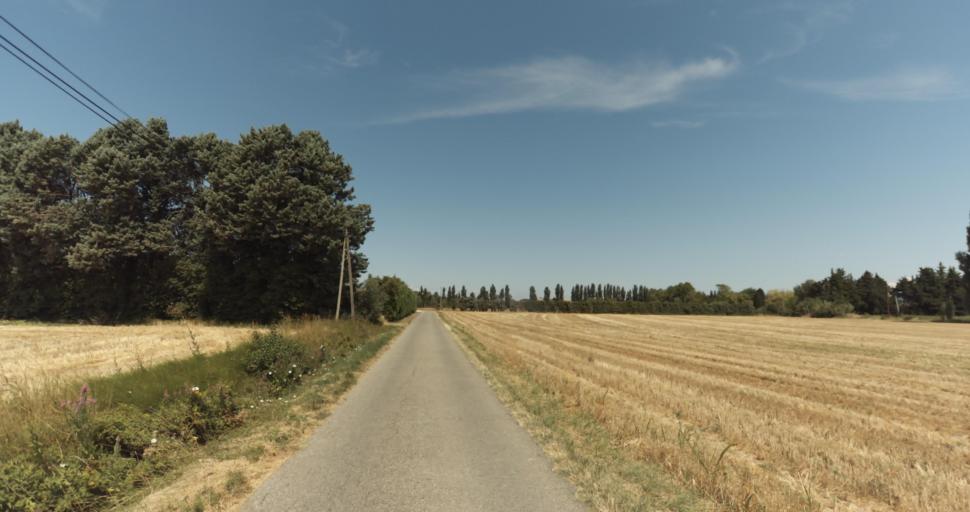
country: FR
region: Provence-Alpes-Cote d'Azur
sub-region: Departement du Vaucluse
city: Althen-des-Paluds
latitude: 44.0114
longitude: 4.9652
